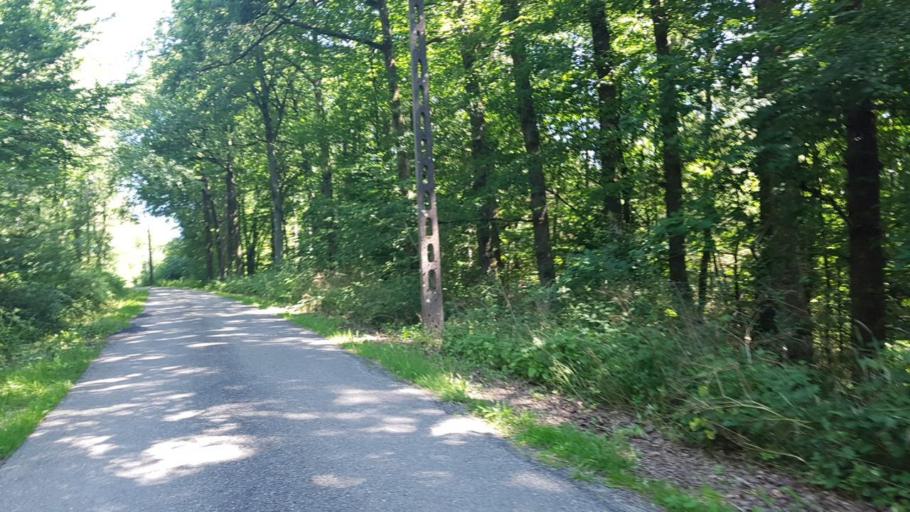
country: BE
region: Wallonia
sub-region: Province du Hainaut
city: Momignies
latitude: 50.1046
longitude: 4.2306
